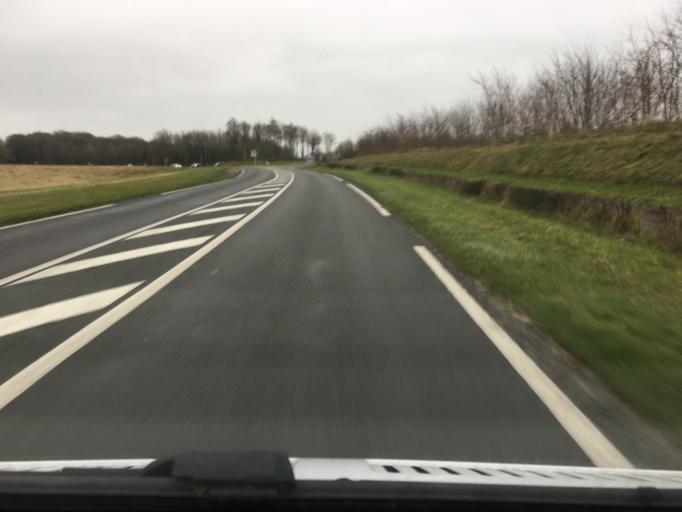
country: FR
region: Picardie
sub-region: Departement de la Somme
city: Pende
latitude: 50.1830
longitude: 1.5935
